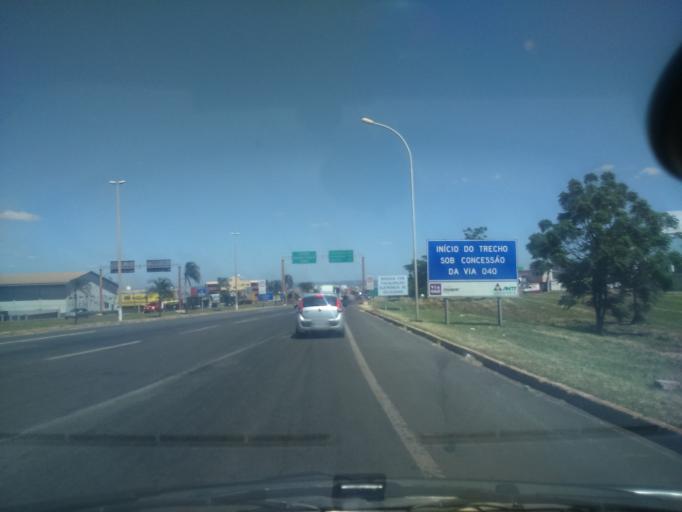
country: BR
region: Goias
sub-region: Luziania
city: Luziania
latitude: -16.0504
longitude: -47.9817
